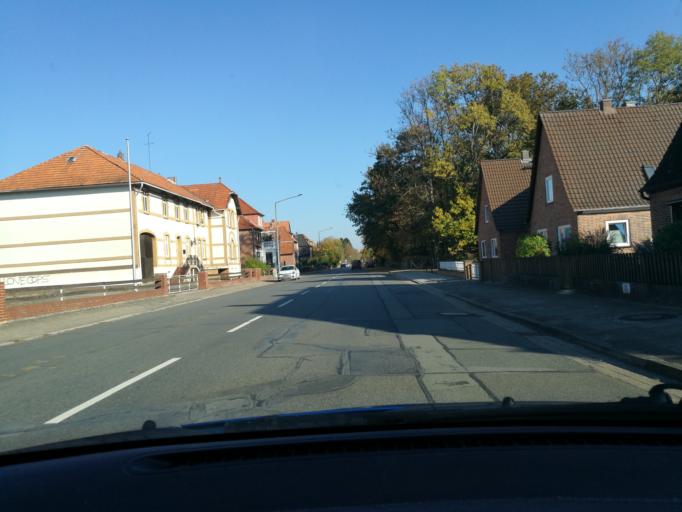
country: DE
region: Lower Saxony
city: Dannenberg
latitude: 53.1030
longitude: 11.1135
